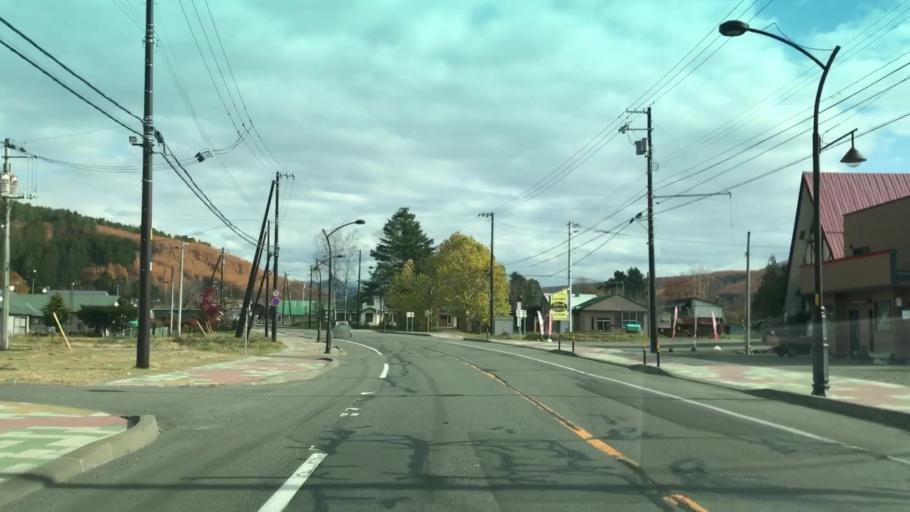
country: JP
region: Hokkaido
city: Shizunai-furukawacho
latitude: 42.7265
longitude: 142.3035
